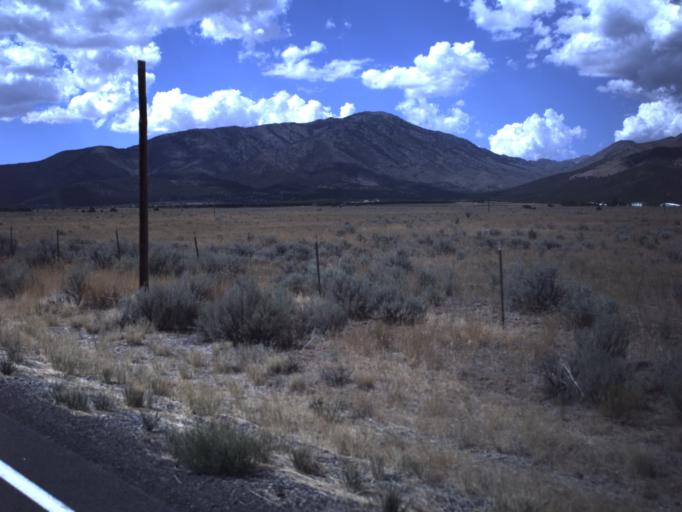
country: US
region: Utah
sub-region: Tooele County
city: Grantsville
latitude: 40.3361
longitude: -112.5008
